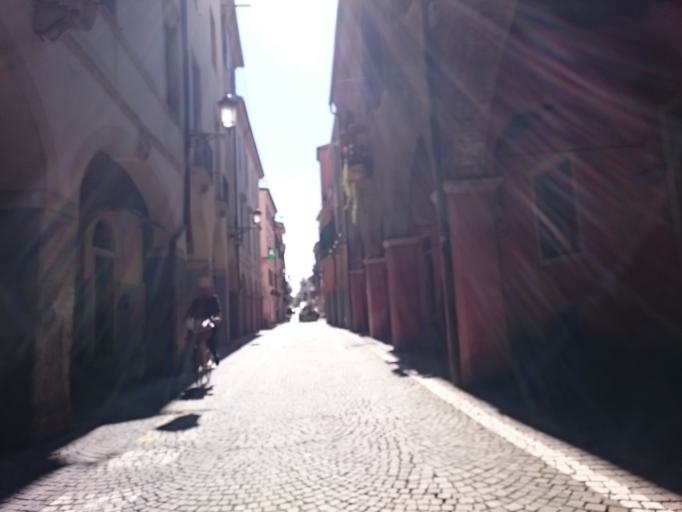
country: IT
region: Veneto
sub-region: Provincia di Padova
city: Padova
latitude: 45.4031
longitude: 11.8830
